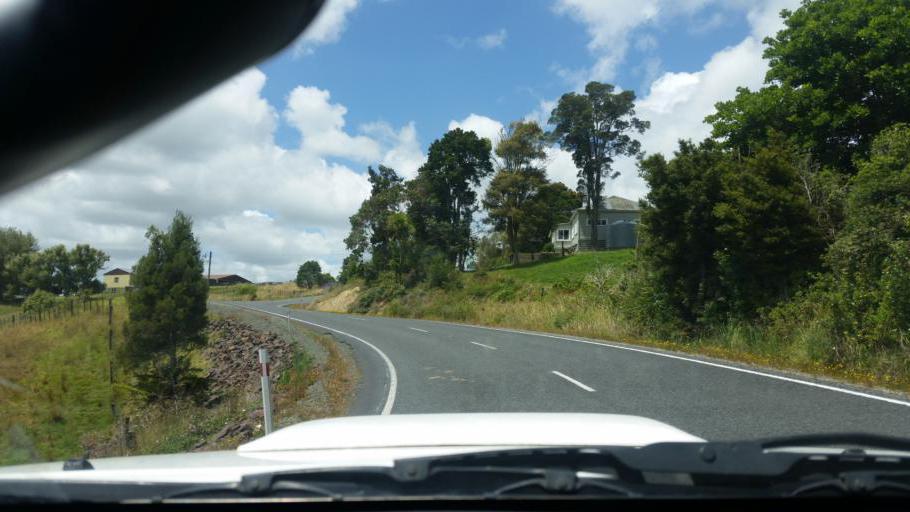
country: NZ
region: Northland
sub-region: Whangarei
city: Ruakaka
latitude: -36.0781
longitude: 174.2432
